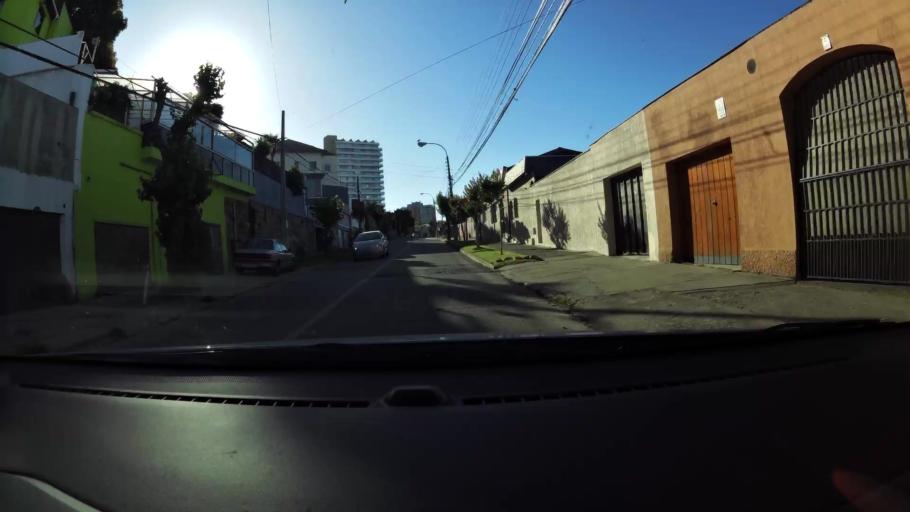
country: CL
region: Valparaiso
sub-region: Provincia de Valparaiso
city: Vina del Mar
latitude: -33.0283
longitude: -71.5796
